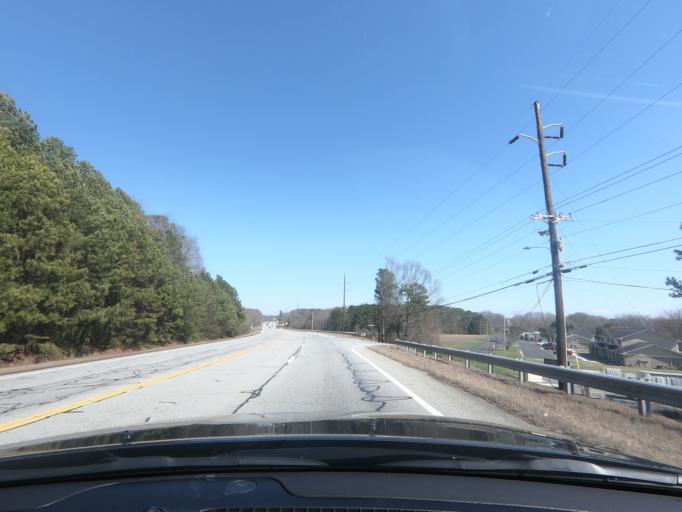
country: US
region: Georgia
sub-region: Gordon County
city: Calhoun
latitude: 34.4727
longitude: -84.9684
